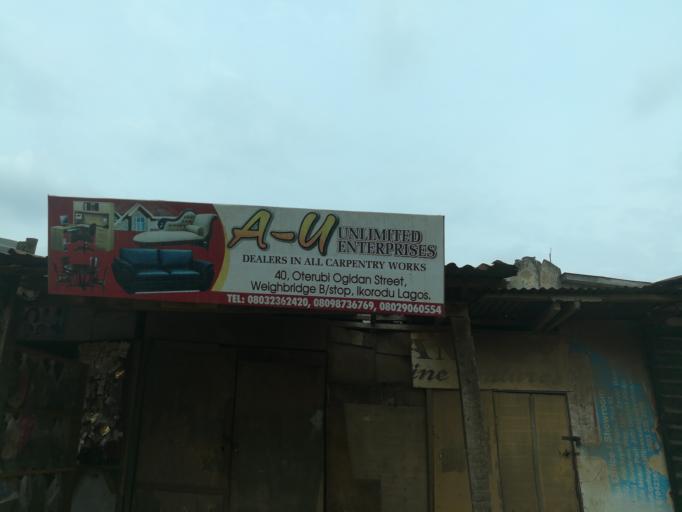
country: NG
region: Lagos
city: Ojota
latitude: 6.6068
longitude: 3.4149
